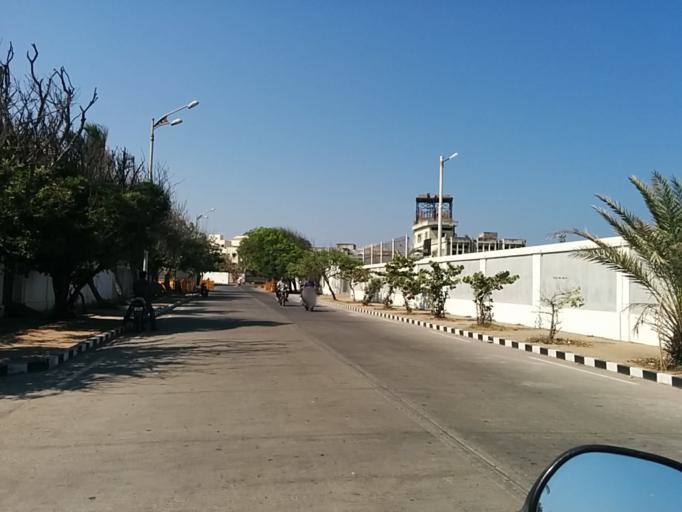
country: IN
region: Pondicherry
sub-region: Puducherry
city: Puducherry
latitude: 11.9378
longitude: 79.8362
